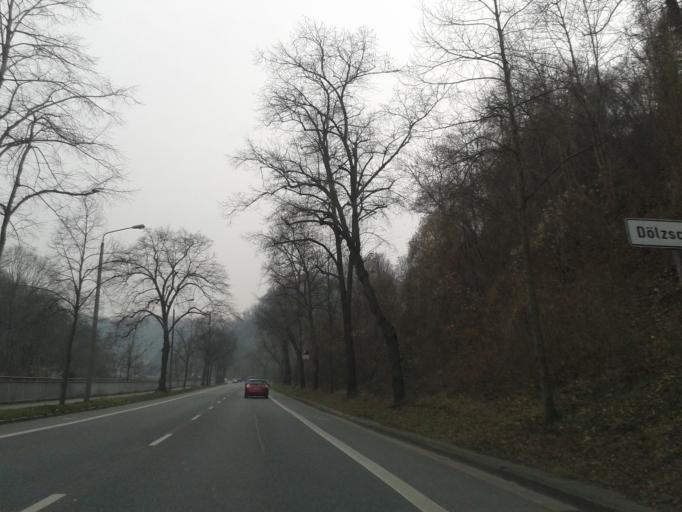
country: DE
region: Saxony
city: Bannewitz
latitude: 51.0287
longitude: 13.7003
